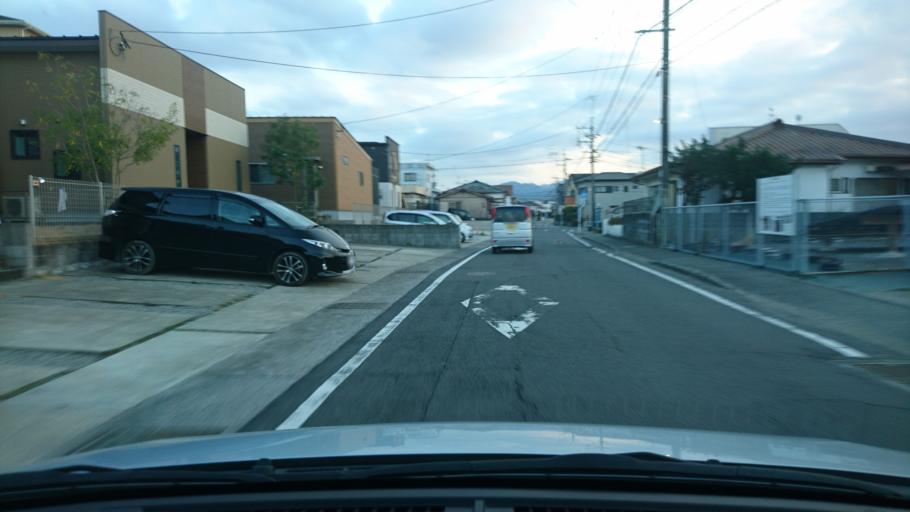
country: JP
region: Miyazaki
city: Miyazaki-shi
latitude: 31.8639
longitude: 131.4271
